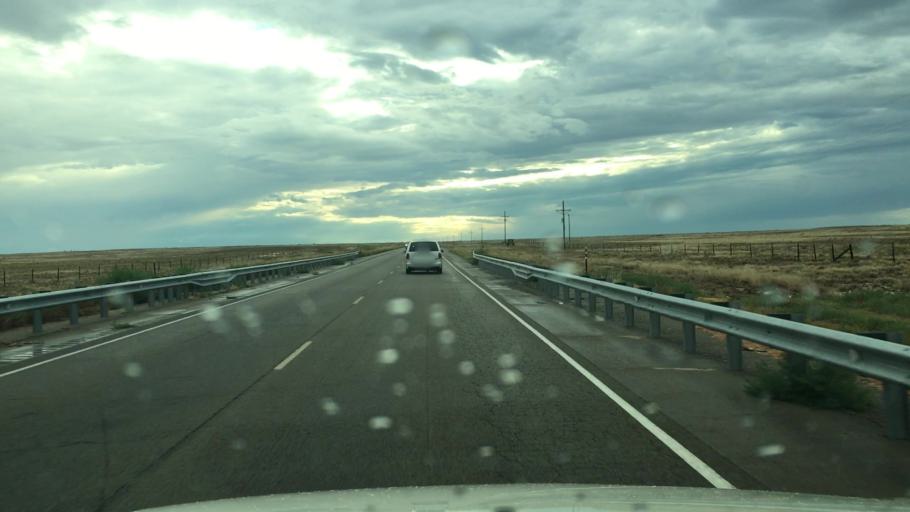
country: US
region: New Mexico
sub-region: Chaves County
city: Roswell
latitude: 33.4056
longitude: -104.3083
